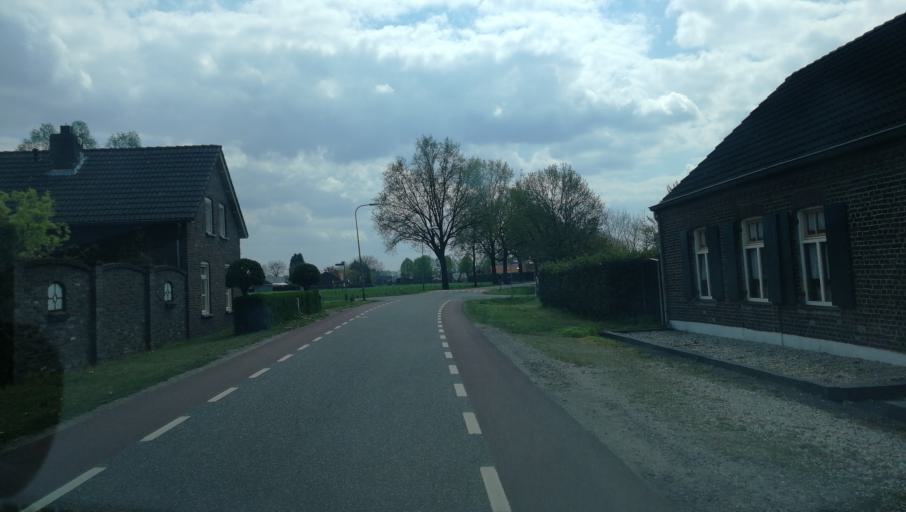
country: NL
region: Limburg
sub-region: Gemeente Peel en Maas
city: Maasbree
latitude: 51.4414
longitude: 6.0276
